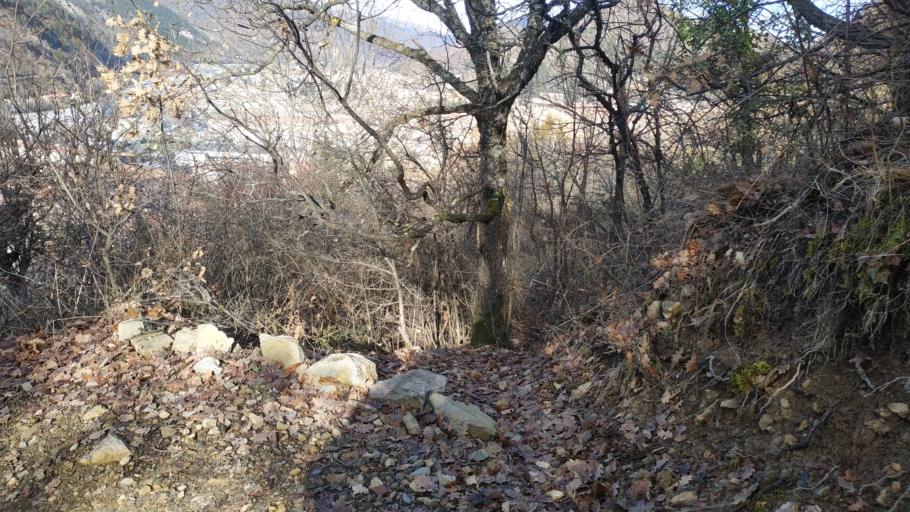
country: FR
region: Provence-Alpes-Cote d'Azur
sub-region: Departement des Alpes-de-Haute-Provence
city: Digne-les-Bains
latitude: 44.0864
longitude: 6.2330
